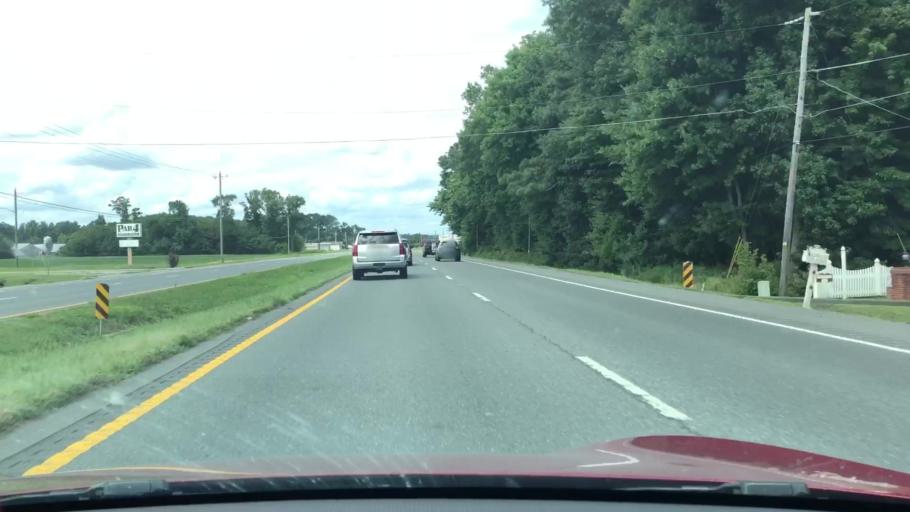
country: US
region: Virginia
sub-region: Accomack County
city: Wattsville
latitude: 37.9035
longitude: -75.5489
